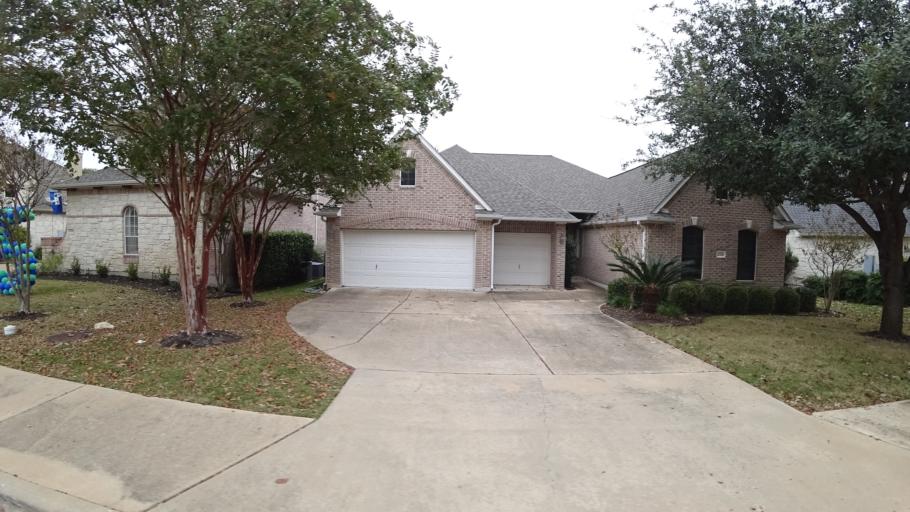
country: US
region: Texas
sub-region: Travis County
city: Bee Cave
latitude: 30.3128
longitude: -97.9257
